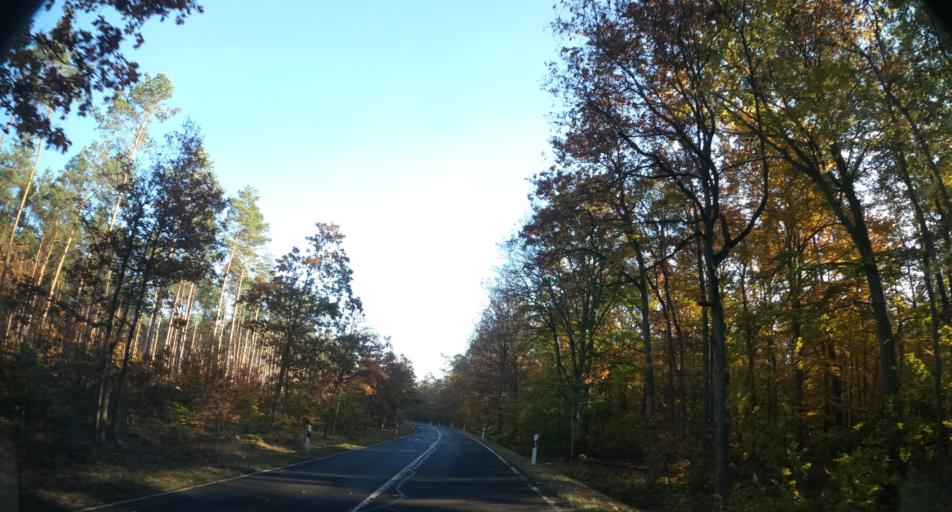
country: PL
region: West Pomeranian Voivodeship
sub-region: Powiat policki
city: Nowe Warpno
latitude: 53.6196
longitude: 14.2884
